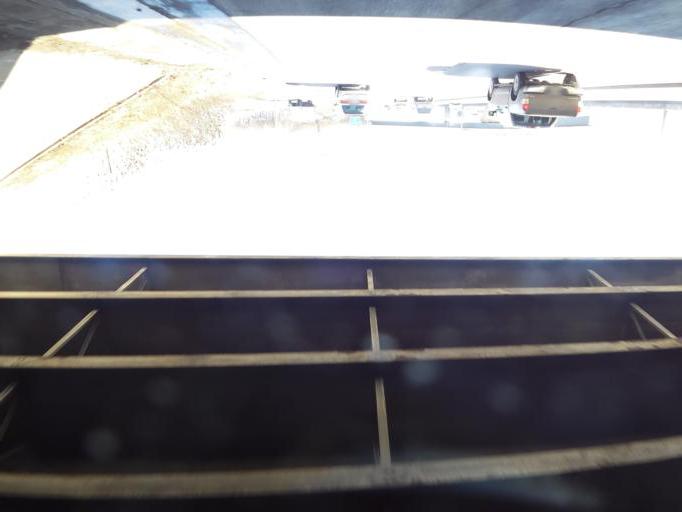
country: US
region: Minnesota
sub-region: Hennepin County
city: Saint Louis Park
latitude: 44.9710
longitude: -93.3409
